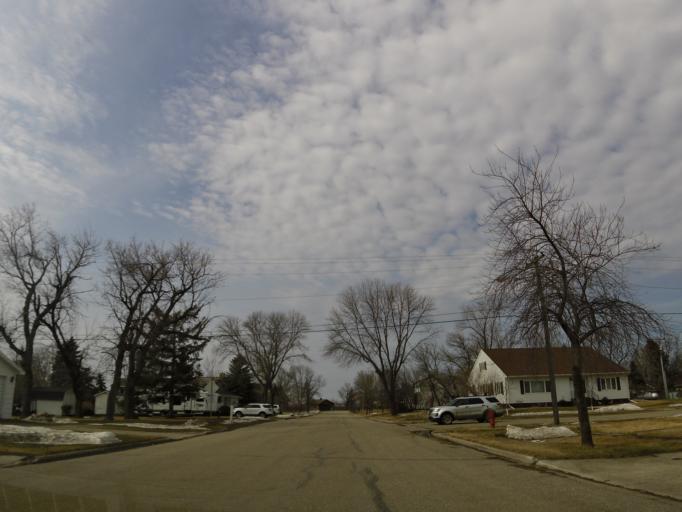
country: US
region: North Dakota
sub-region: Walsh County
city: Grafton
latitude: 48.2895
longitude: -97.3725
